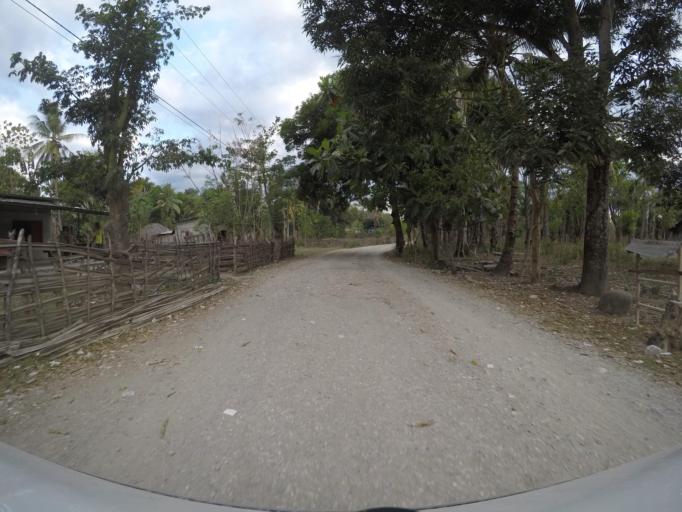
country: TL
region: Bobonaro
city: Maliana
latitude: -8.8742
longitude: 125.2124
